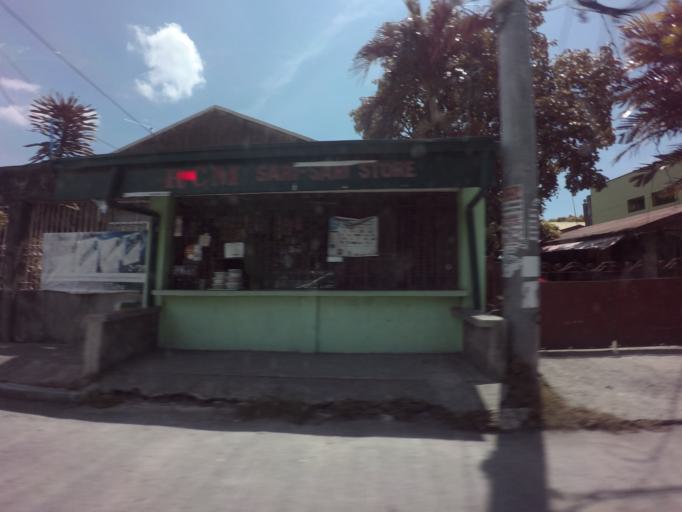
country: PH
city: Sambayanihan People's Village
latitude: 14.4238
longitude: 121.0123
